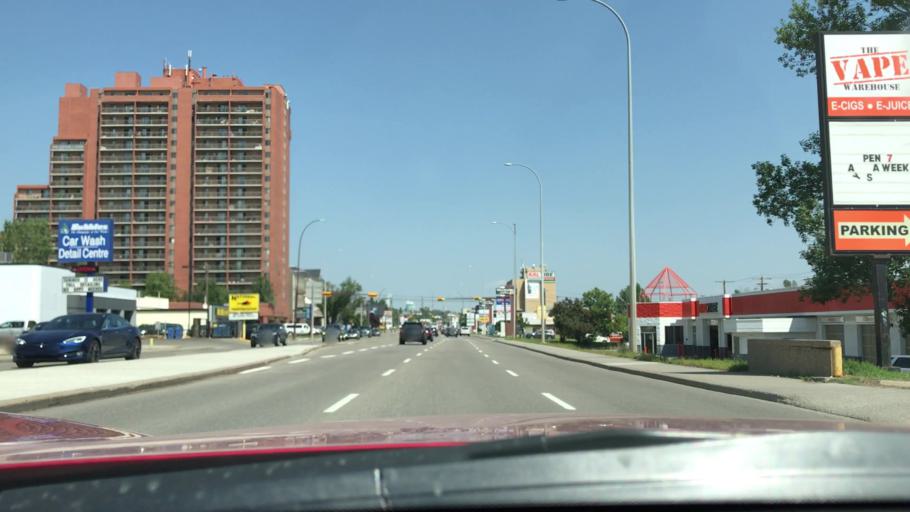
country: CA
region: Alberta
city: Calgary
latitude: 51.0102
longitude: -114.0670
